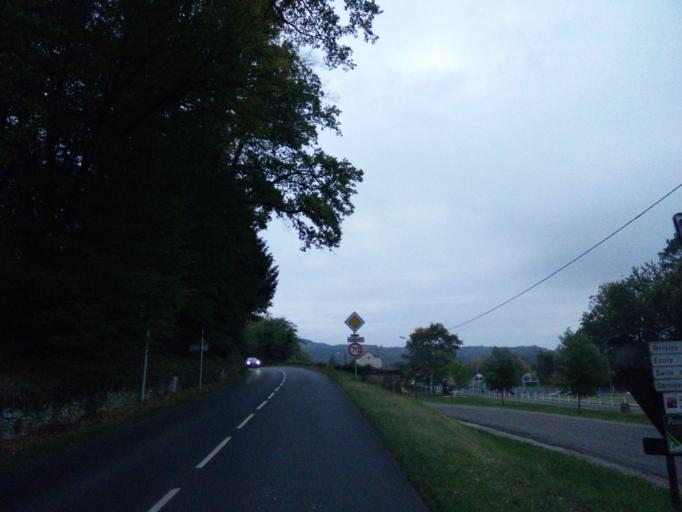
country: FR
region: Aquitaine
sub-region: Departement de la Dordogne
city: Carsac-Aillac
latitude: 44.8367
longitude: 1.2752
